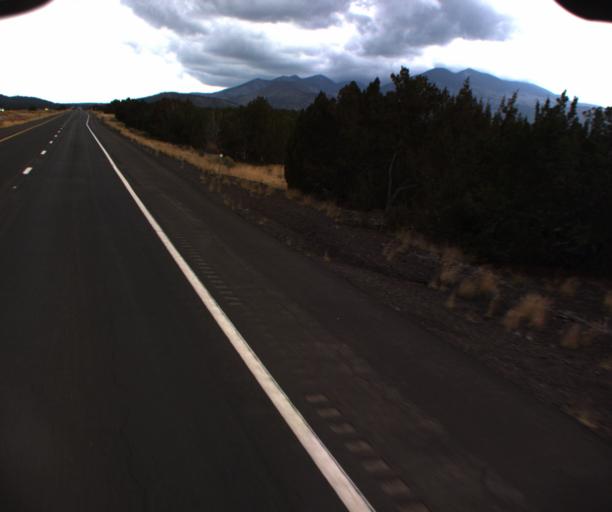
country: US
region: Arizona
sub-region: Coconino County
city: Flagstaff
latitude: 35.4246
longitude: -111.5700
